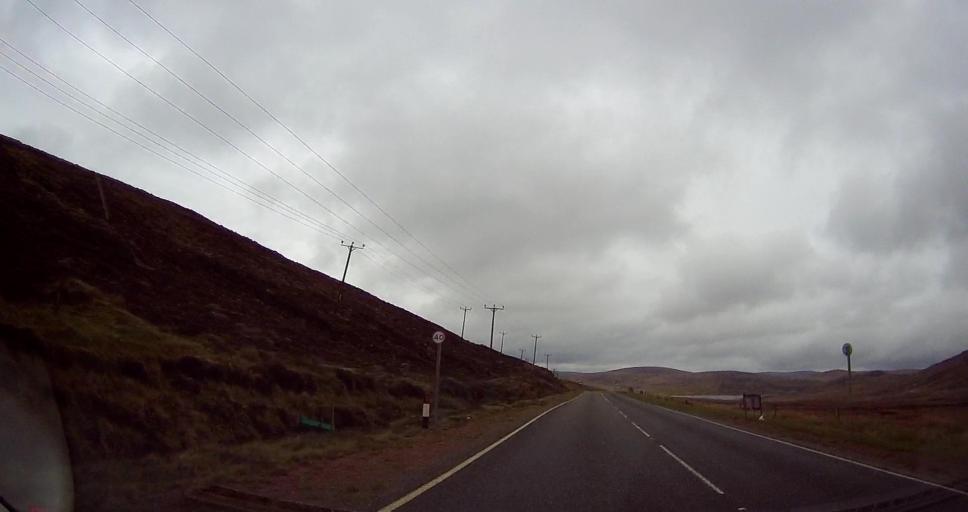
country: GB
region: Scotland
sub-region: Shetland Islands
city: Lerwick
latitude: 60.3302
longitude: -1.2540
